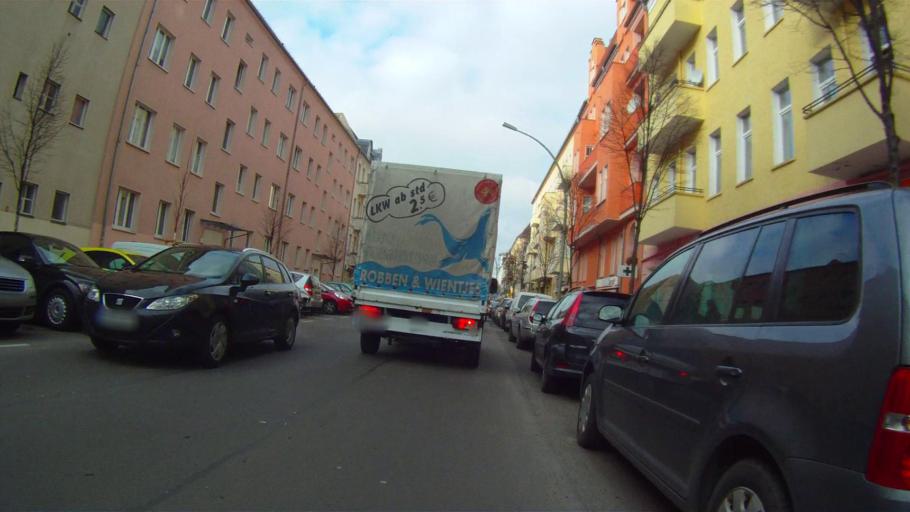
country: DE
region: Berlin
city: Lichtenberg
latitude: 52.5092
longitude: 13.5013
